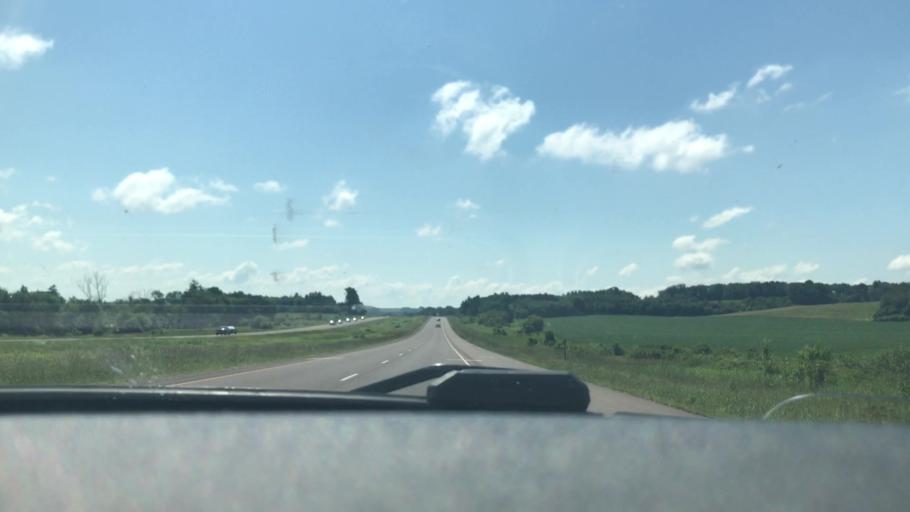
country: US
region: Wisconsin
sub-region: Chippewa County
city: Bloomer
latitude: 45.0820
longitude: -91.4826
